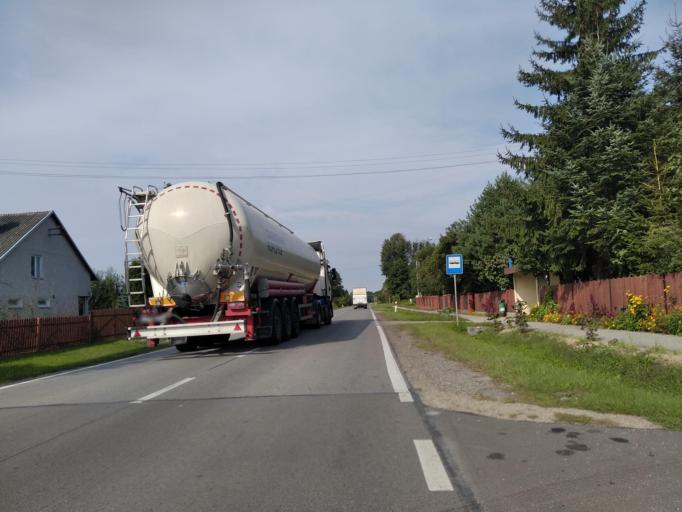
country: PL
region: Subcarpathian Voivodeship
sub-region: Powiat mielecki
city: Przeclaw
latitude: 50.1623
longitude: 21.5253
